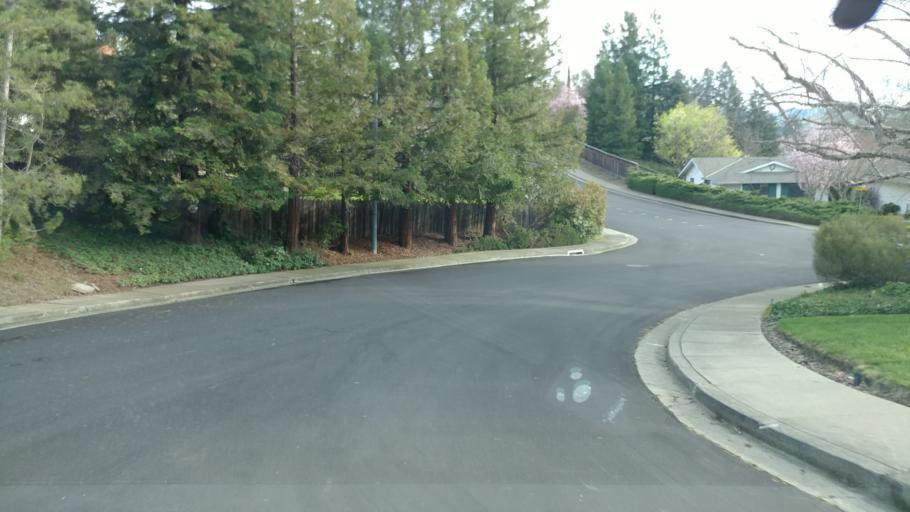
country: US
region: California
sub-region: Contra Costa County
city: Danville
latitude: 37.8240
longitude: -121.9789
